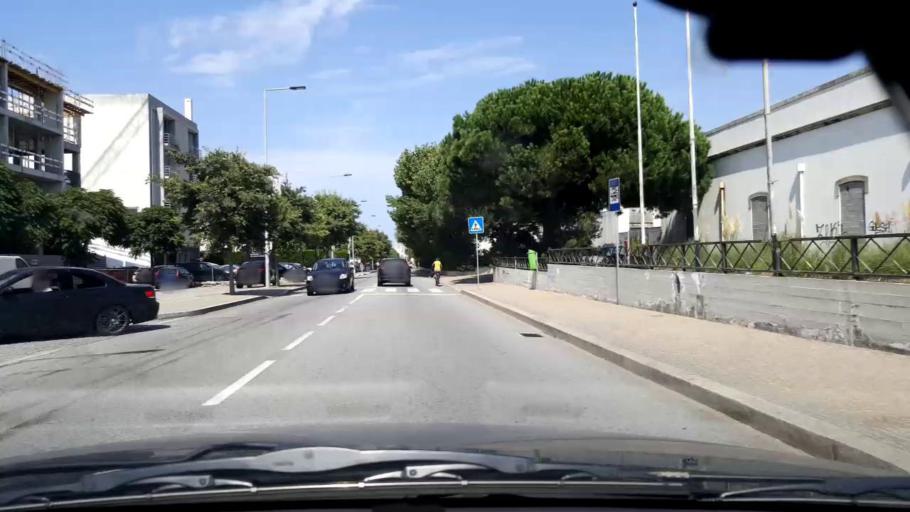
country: PT
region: Porto
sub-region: Povoa de Varzim
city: Povoa de Varzim
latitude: 41.3706
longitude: -8.7529
